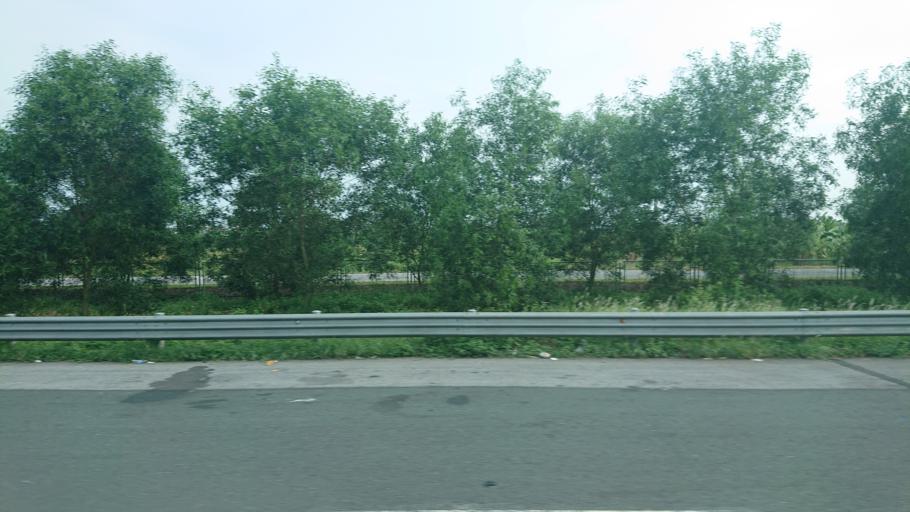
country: VN
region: Hai Phong
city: An Lao
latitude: 20.8158
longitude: 106.4913
